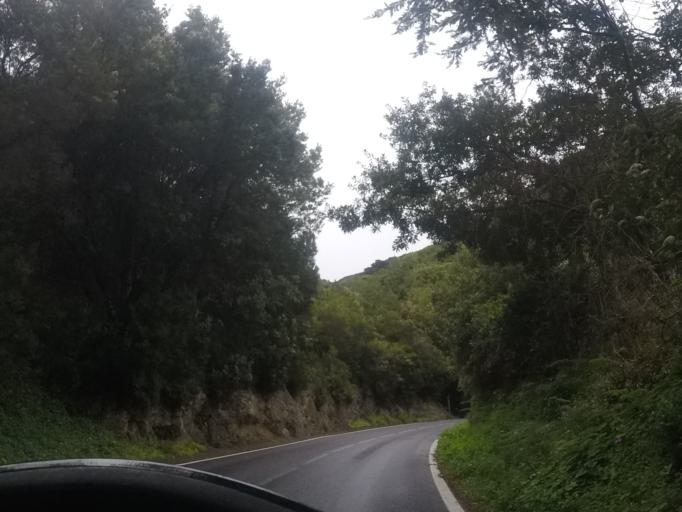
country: ES
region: Canary Islands
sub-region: Provincia de Santa Cruz de Tenerife
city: Tegueste
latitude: 28.5267
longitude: -16.2873
